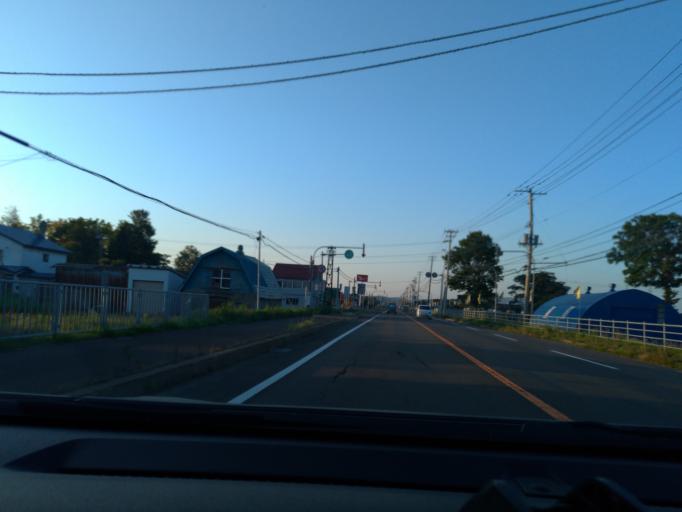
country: JP
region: Hokkaido
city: Tobetsu
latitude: 43.1992
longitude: 141.5222
